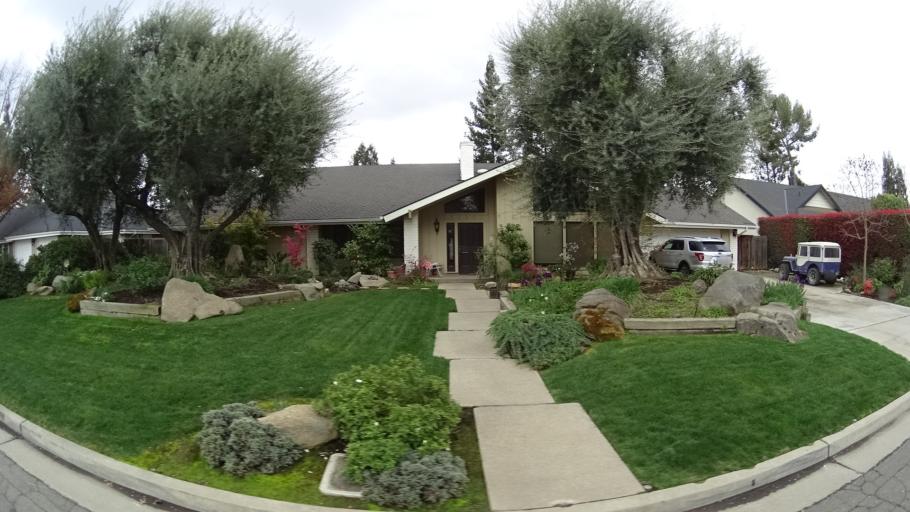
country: US
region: California
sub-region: Fresno County
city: Fresno
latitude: 36.8413
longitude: -119.8283
